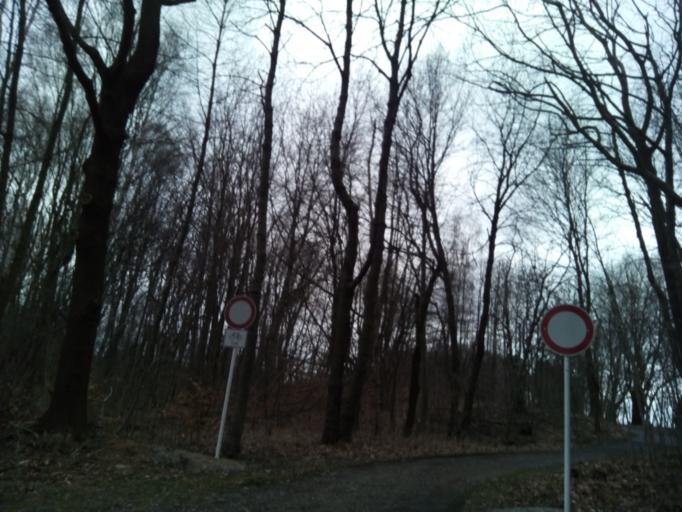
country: DE
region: Saxony
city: Brand-Erbisdorf
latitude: 50.8824
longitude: 13.3304
